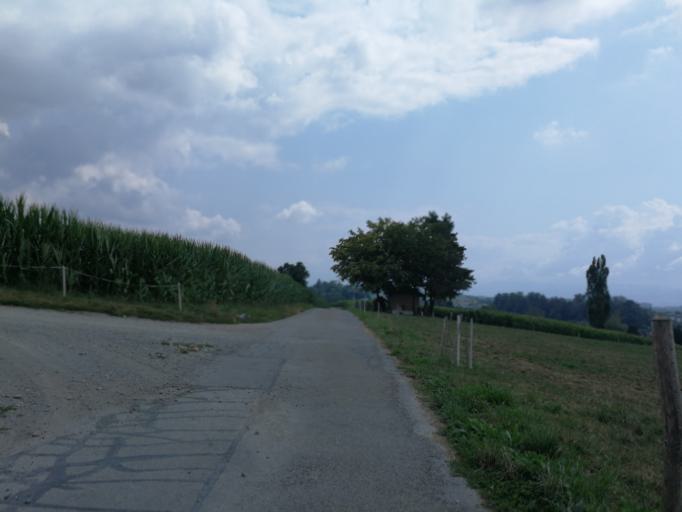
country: CH
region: Zurich
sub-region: Bezirk Hinwil
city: Gossau
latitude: 47.3110
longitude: 8.7624
